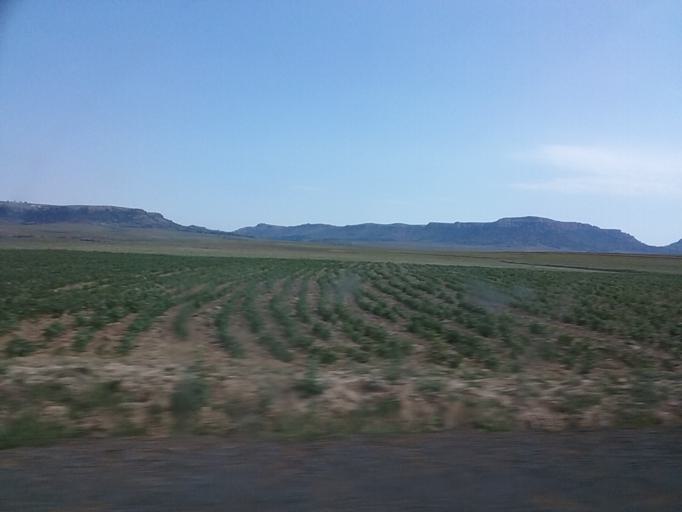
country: LS
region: Berea
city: Teyateyaneng
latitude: -29.0832
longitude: 27.9010
